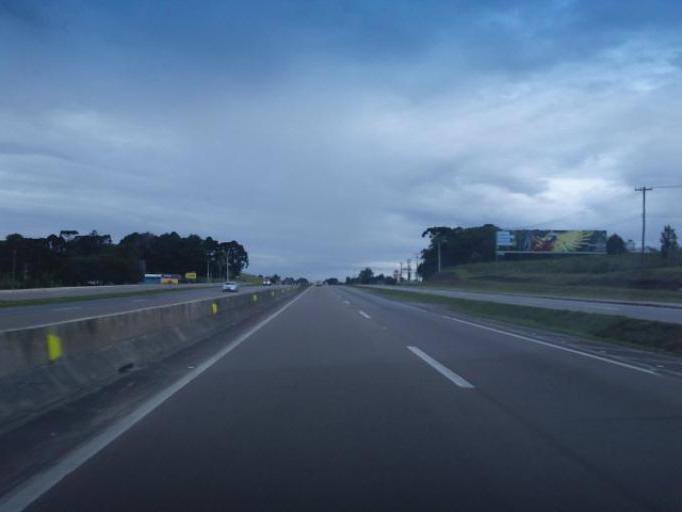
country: BR
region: Parana
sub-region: Sao Jose Dos Pinhais
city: Sao Jose dos Pinhais
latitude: -25.6723
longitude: -49.1514
